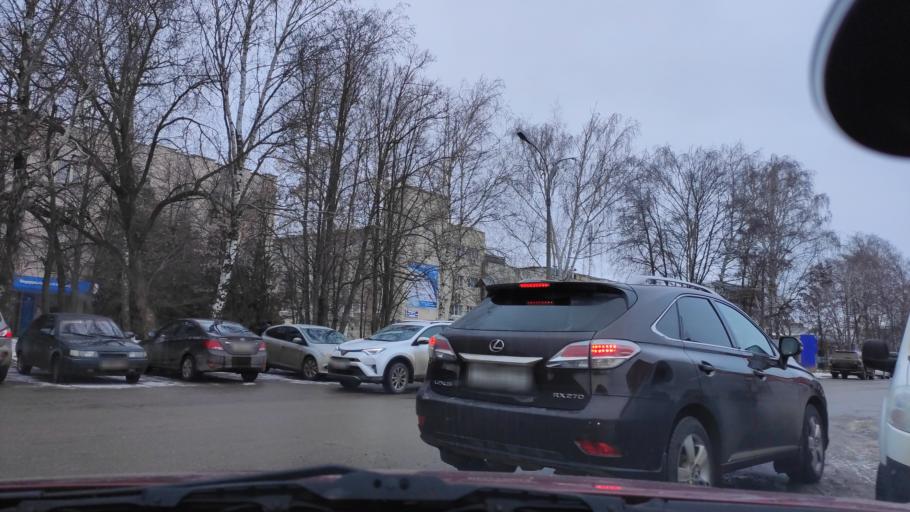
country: RU
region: Tambov
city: Tambov
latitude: 52.7547
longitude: 41.4539
